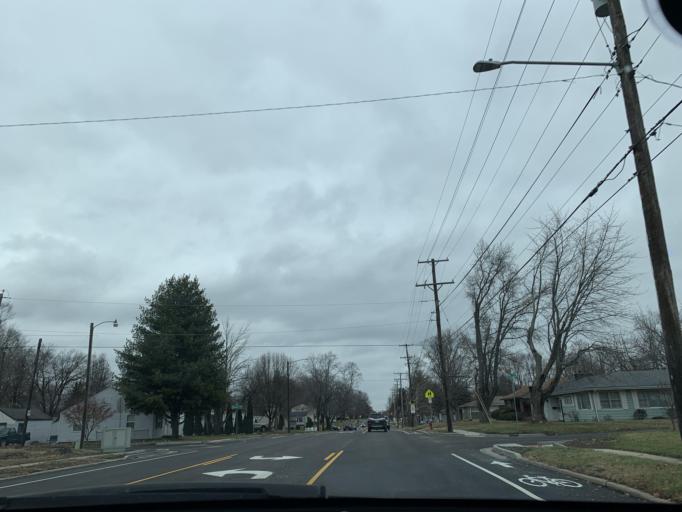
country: US
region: Illinois
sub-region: Sangamon County
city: Leland Grove
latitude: 39.8120
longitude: -89.6871
